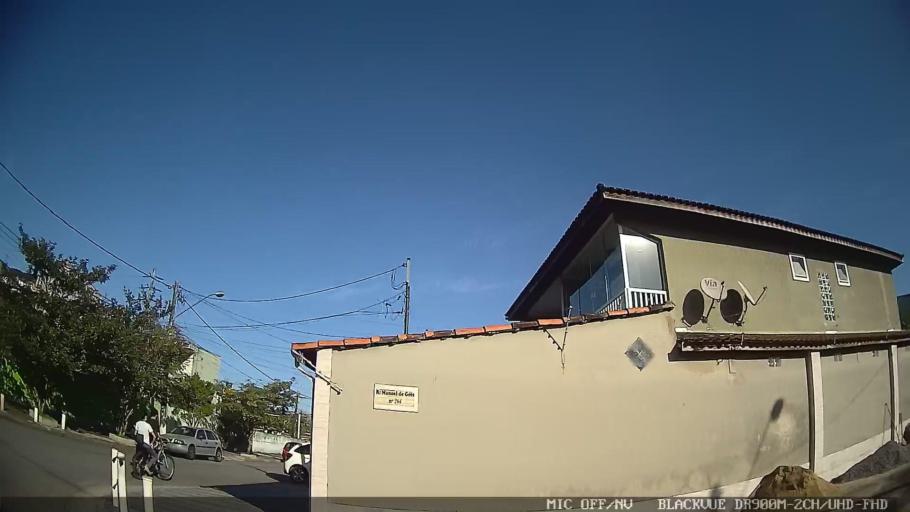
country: BR
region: Sao Paulo
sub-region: Guaruja
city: Guaruja
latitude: -23.9612
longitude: -46.2823
